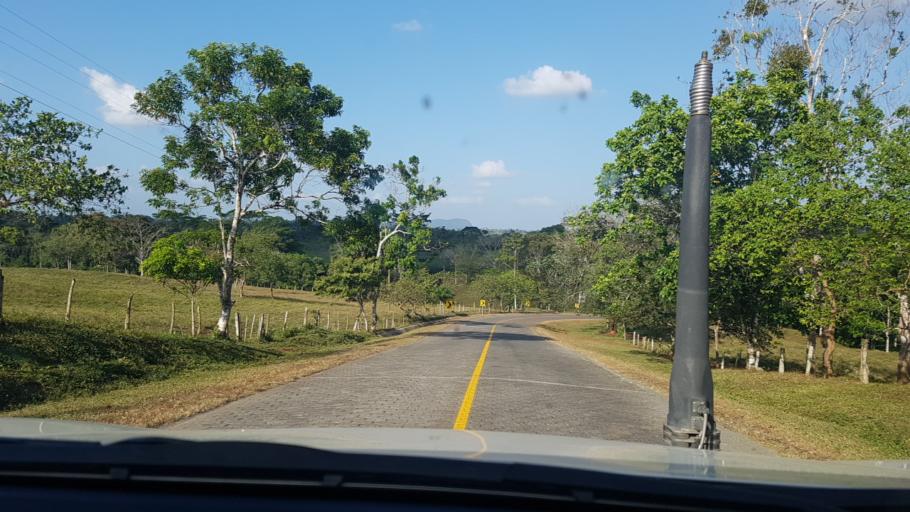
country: NI
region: Atlantico Sur
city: Nueva Guinea
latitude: 11.6944
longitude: -84.4134
